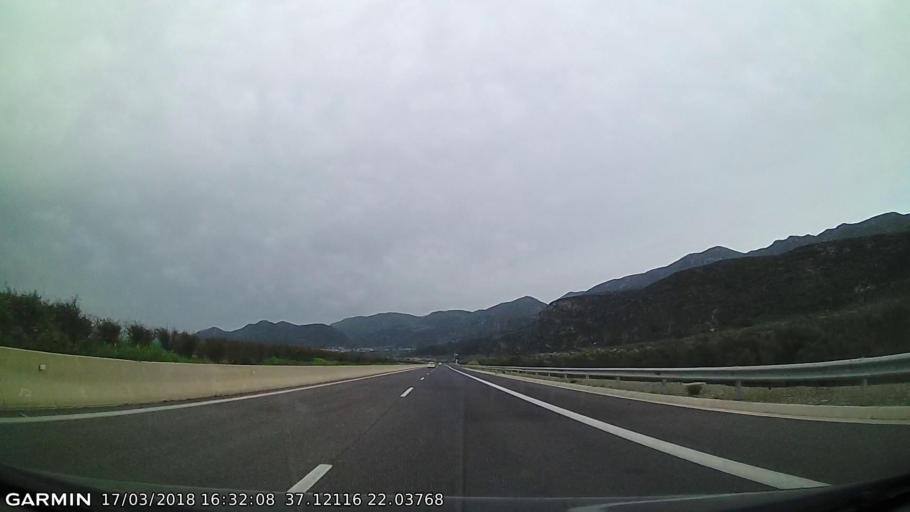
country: GR
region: Peloponnese
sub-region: Nomos Messinias
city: Arfara
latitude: 37.1215
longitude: 22.0379
